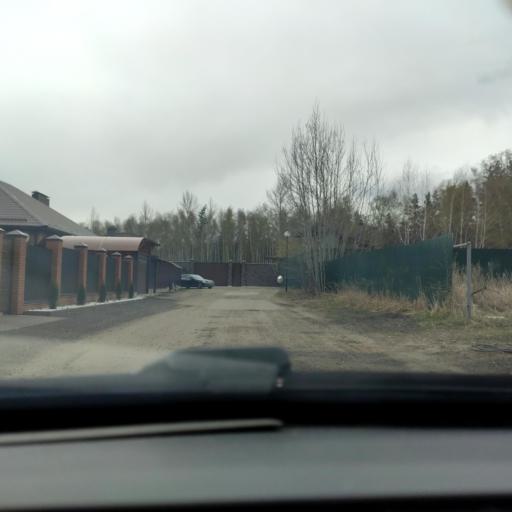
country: RU
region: Voronezj
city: Podgornoye
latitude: 51.7556
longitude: 39.1503
